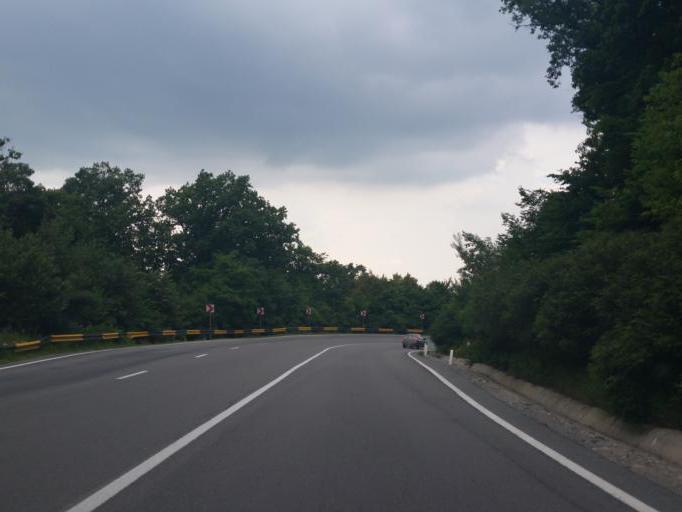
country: RO
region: Salaj
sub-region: Comuna Treznea
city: Treznea
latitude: 47.1525
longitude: 23.0923
